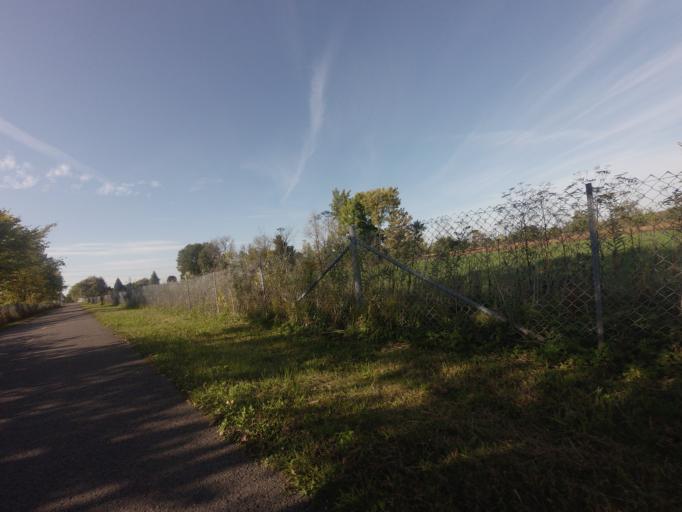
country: CA
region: Quebec
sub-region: Laurentides
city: Blainville
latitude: 45.7215
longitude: -73.9314
